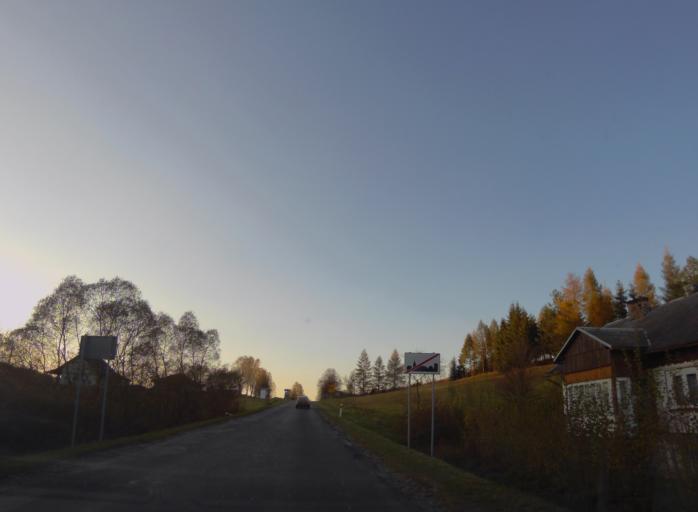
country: PL
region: Subcarpathian Voivodeship
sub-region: Powiat leski
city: Polanczyk
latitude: 49.3960
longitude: 22.3820
